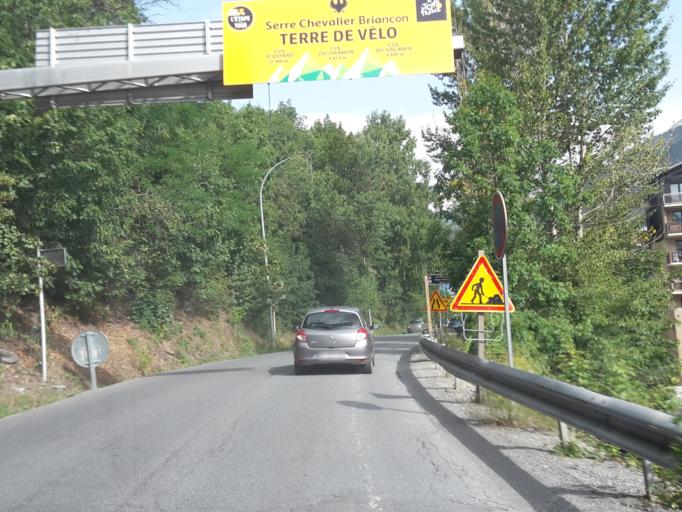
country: FR
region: Provence-Alpes-Cote d'Azur
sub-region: Departement des Hautes-Alpes
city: Briancon
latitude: 44.8953
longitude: 6.6298
